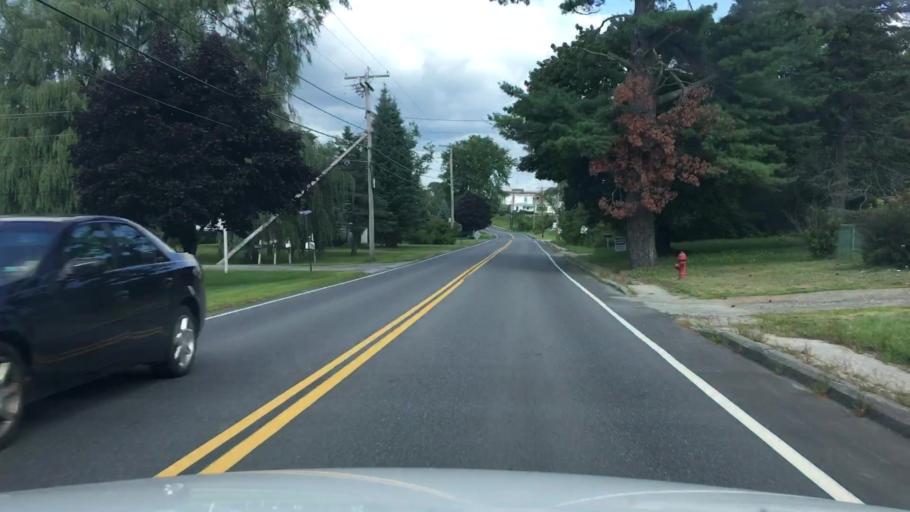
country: US
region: Maine
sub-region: Somerset County
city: Skowhegan
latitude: 44.7552
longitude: -69.7107
